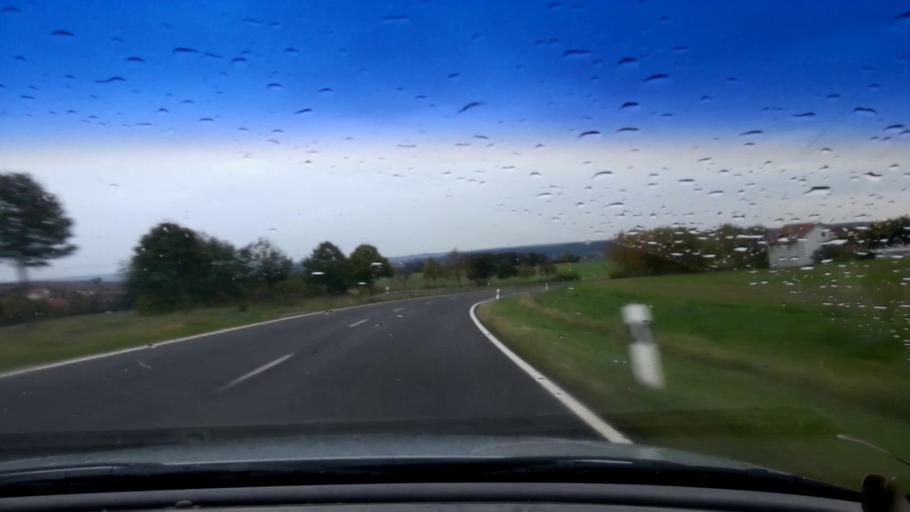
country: DE
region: Bavaria
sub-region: Upper Franconia
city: Priesendorf
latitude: 49.8666
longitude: 10.7175
